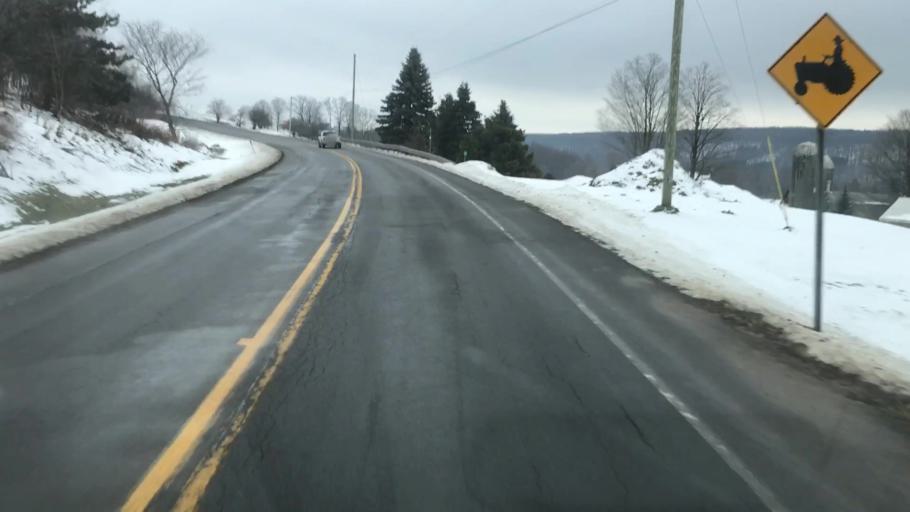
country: US
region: New York
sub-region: Cayuga County
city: Moravia
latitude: 42.6942
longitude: -76.3051
